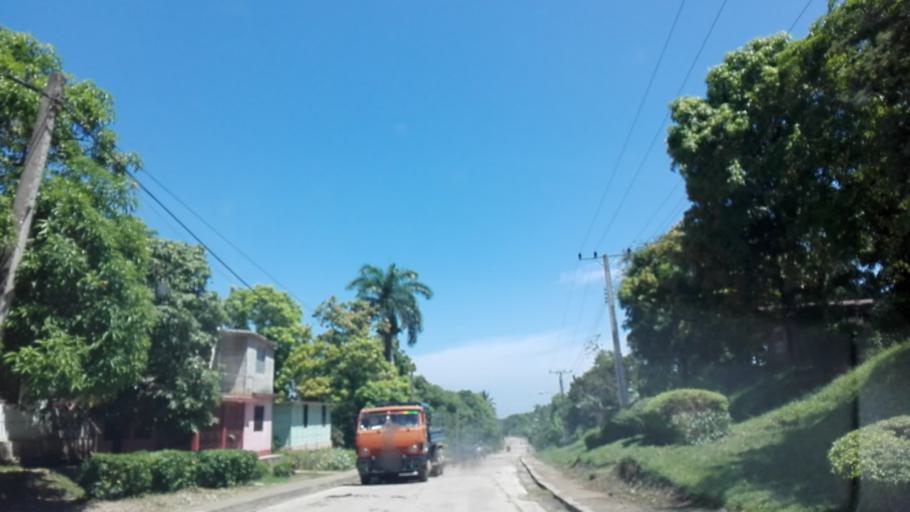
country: CU
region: Granma
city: Bartolome Maso
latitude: 20.1582
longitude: -76.9490
